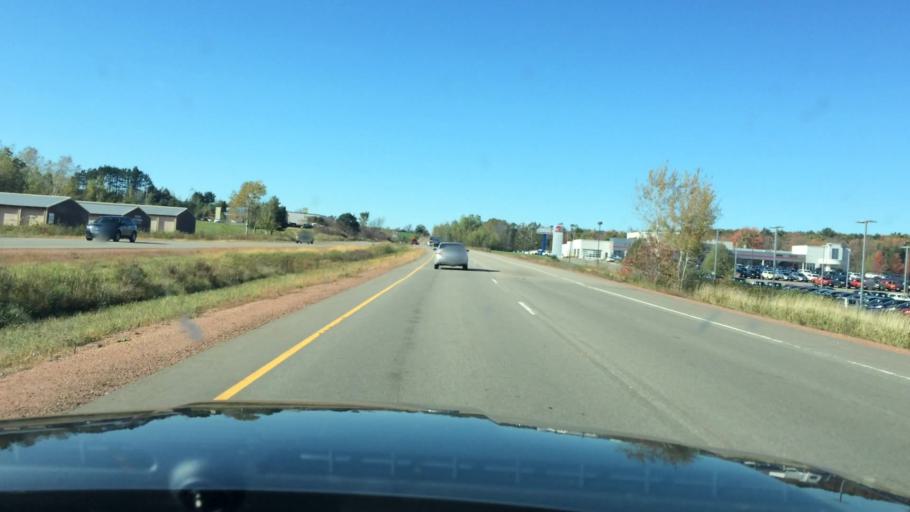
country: US
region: Wisconsin
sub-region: Marathon County
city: Wausau
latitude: 44.9960
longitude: -89.6630
